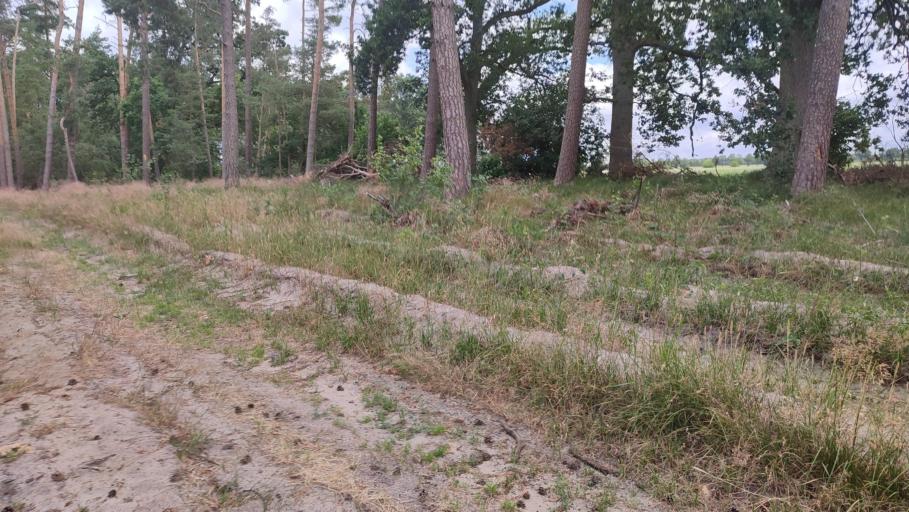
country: DE
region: Lower Saxony
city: Hitzacker
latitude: 53.1958
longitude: 11.0950
